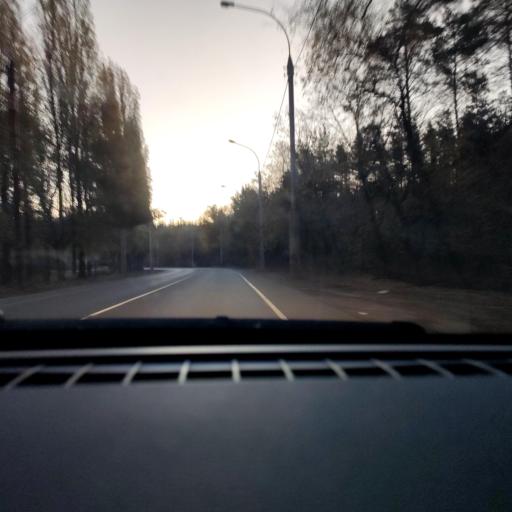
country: RU
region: Voronezj
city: Somovo
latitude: 51.7022
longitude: 39.2868
